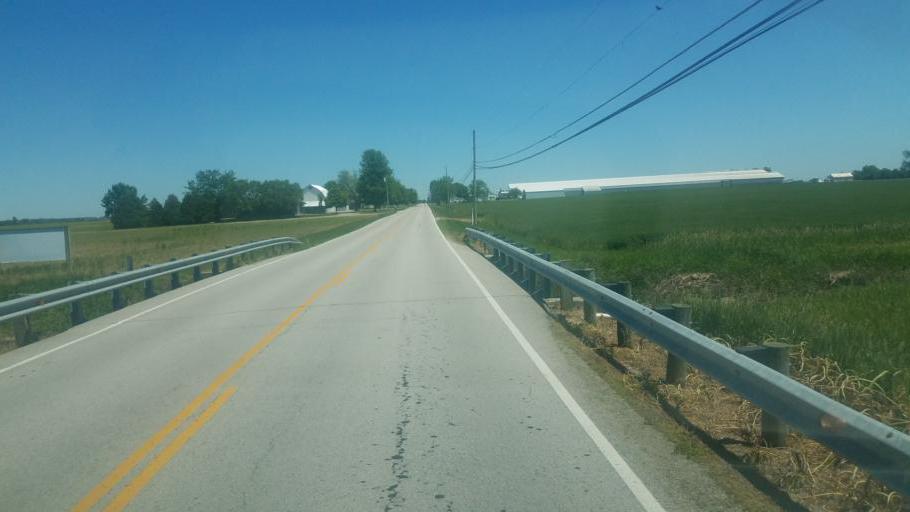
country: US
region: Ohio
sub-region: Darke County
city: Versailles
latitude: 40.2263
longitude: -84.4435
